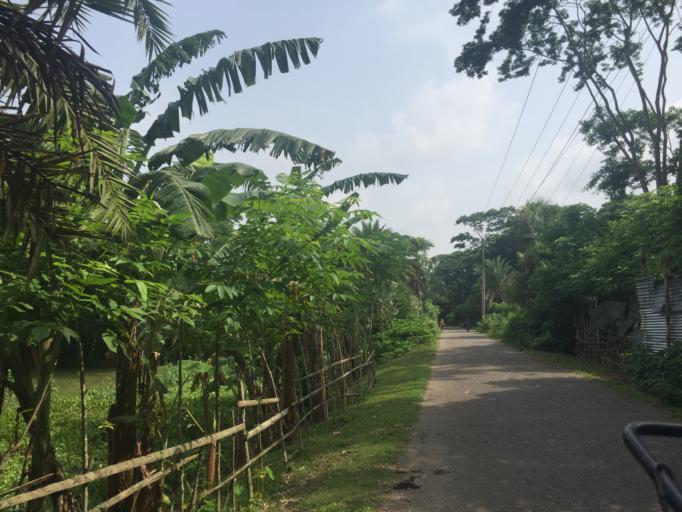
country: BD
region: Barisal
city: Mathba
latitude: 22.2228
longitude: 89.9163
